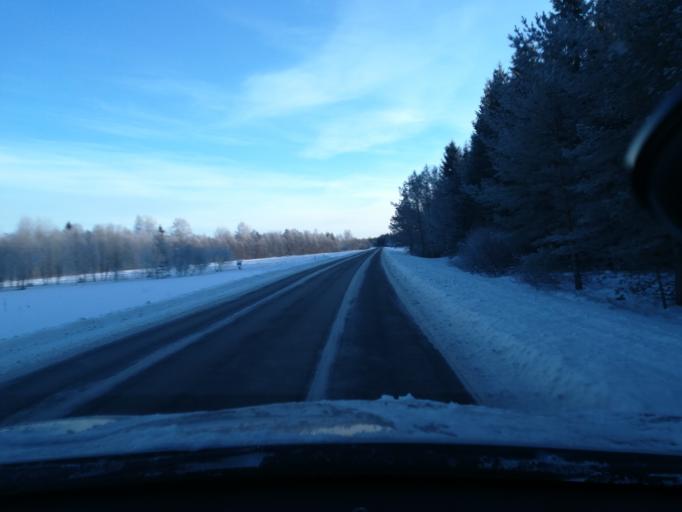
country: EE
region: Harju
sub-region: Keila linn
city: Keila
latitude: 59.3800
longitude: 24.4520
